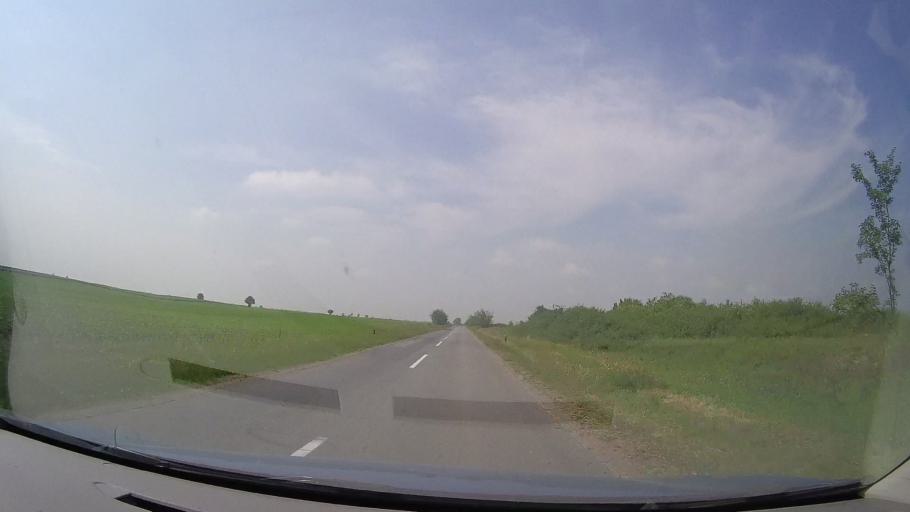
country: RS
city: Padina
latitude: 45.1517
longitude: 20.7453
